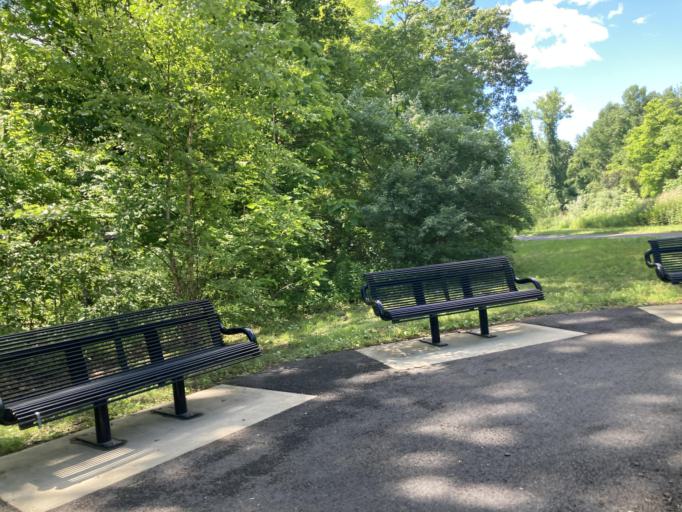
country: US
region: Connecticut
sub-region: New Haven County
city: Wallingford
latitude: 41.4869
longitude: -72.8195
